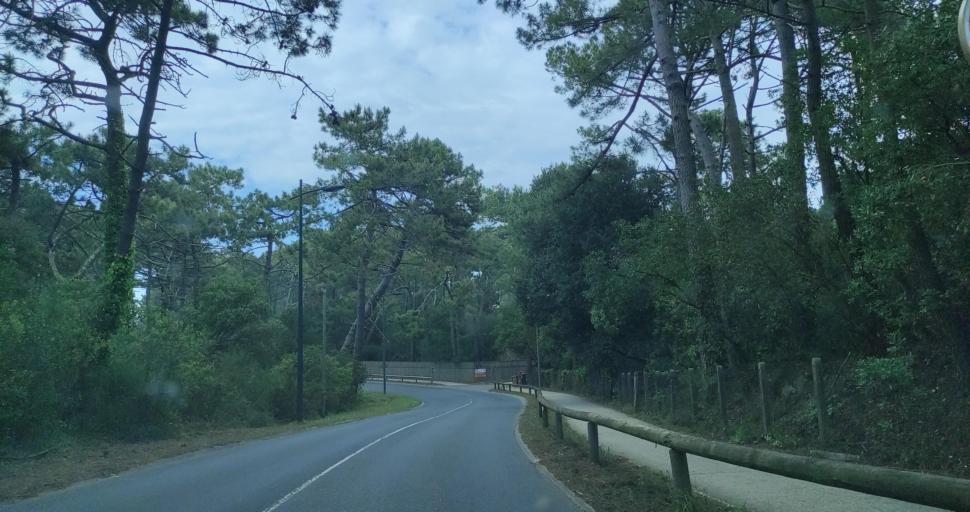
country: FR
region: Aquitaine
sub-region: Departement de la Gironde
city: Arcachon
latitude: 44.6791
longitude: -1.2393
